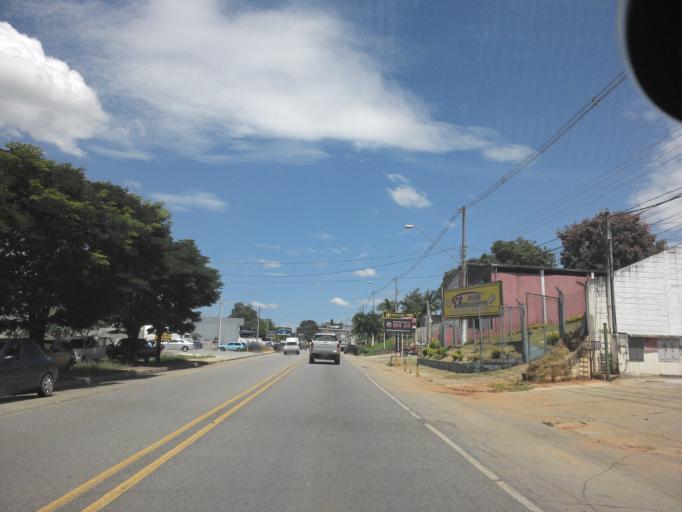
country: BR
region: Sao Paulo
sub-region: Taubate
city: Taubate
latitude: -23.0546
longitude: -45.5554
